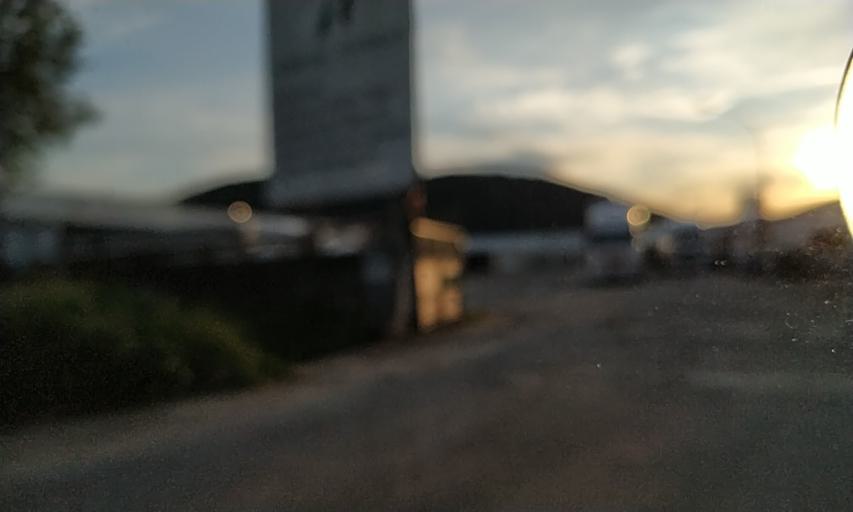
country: ES
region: Galicia
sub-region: Provincia de Ourense
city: Verin
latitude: 41.9198
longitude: -7.4439
